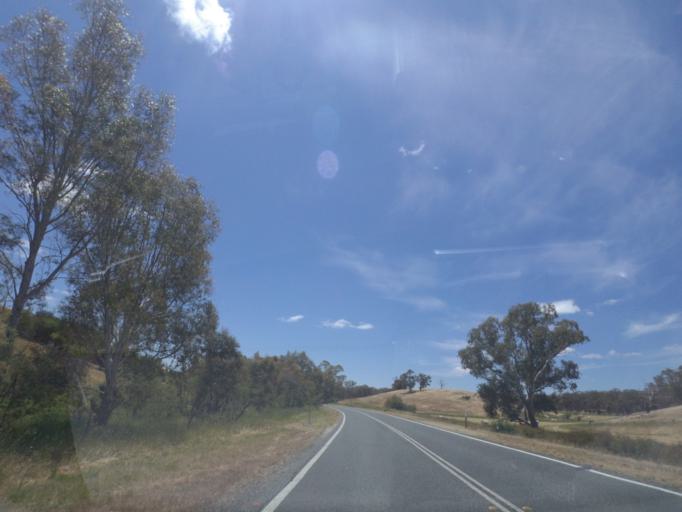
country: AU
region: Victoria
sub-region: Mount Alexander
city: Castlemaine
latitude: -37.1911
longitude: 144.1491
